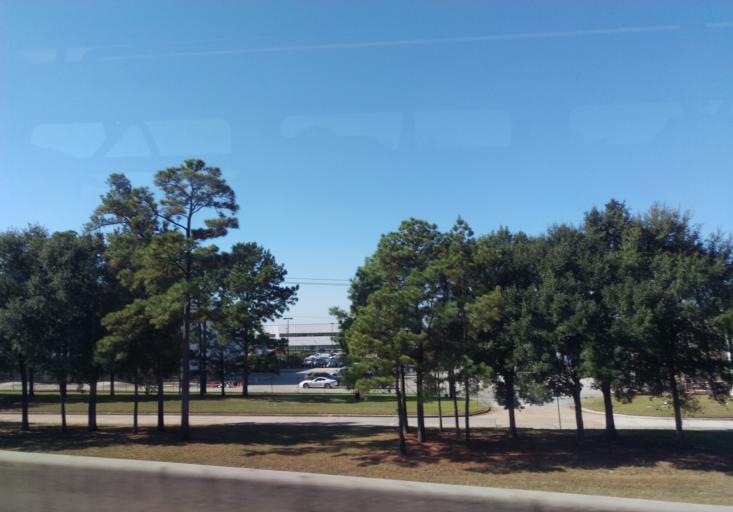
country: US
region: Texas
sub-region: Harris County
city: Aldine
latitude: 29.9710
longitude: -95.3396
